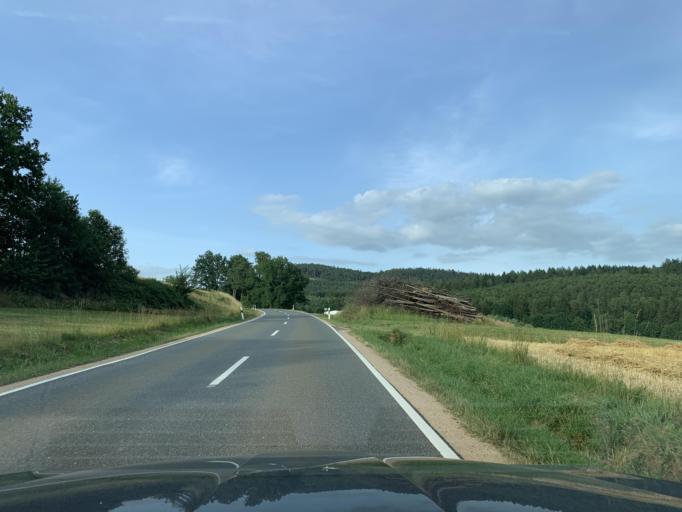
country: DE
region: Bavaria
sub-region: Upper Palatinate
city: Schwarzhofen
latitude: 49.3891
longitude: 12.3553
